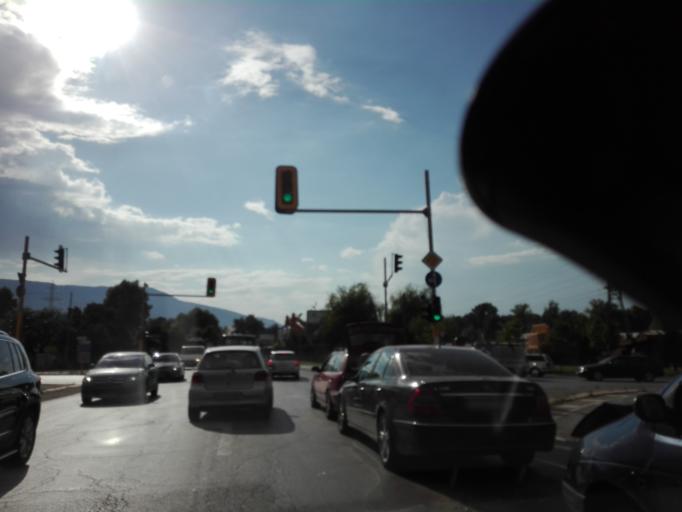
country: BG
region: Sofia-Capital
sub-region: Stolichna Obshtina
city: Sofia
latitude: 42.6219
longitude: 23.4211
